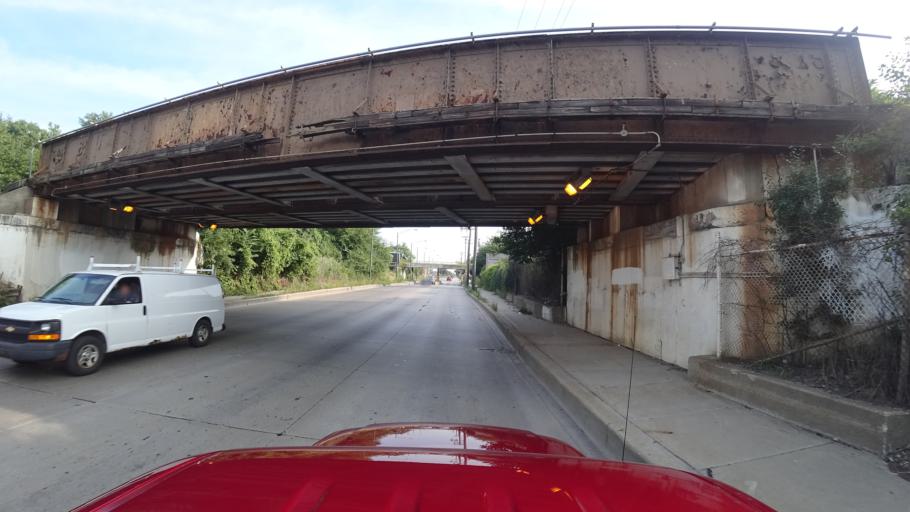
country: US
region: Illinois
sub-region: Cook County
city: Cicero
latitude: 41.8327
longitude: -87.7046
